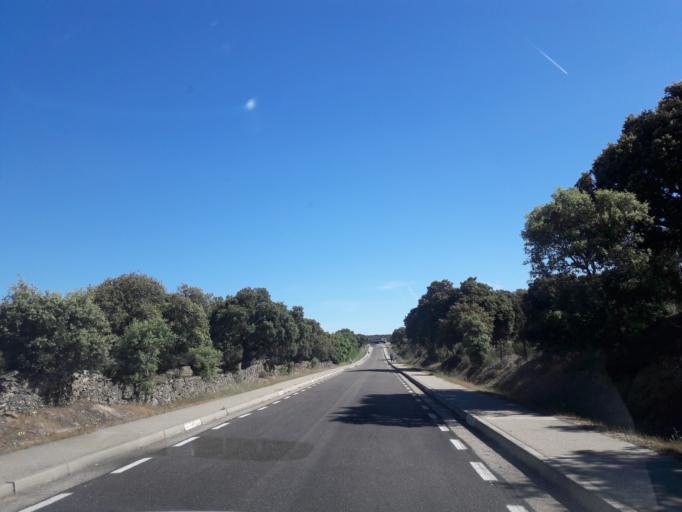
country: ES
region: Castille and Leon
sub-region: Provincia de Salamanca
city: Juzbado
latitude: 41.0821
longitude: -5.8964
